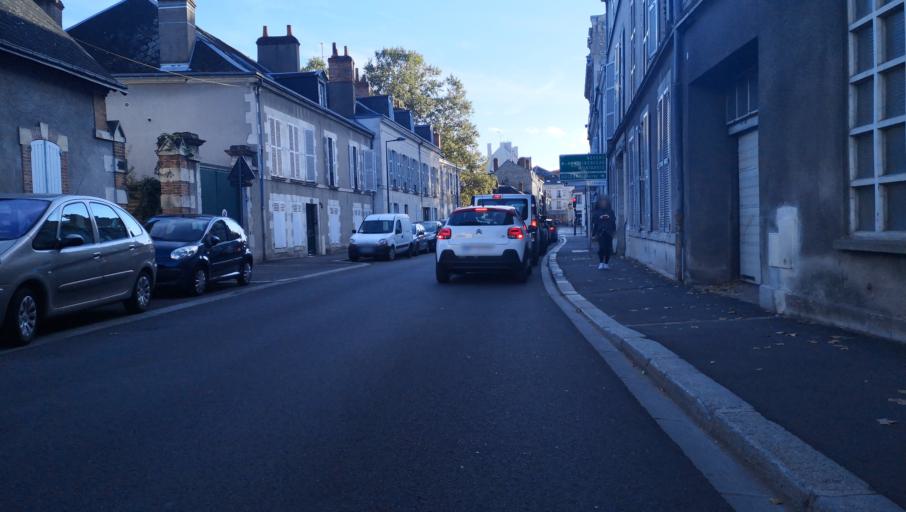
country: FR
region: Centre
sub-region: Departement du Loiret
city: Orleans
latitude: 47.9056
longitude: 1.9139
